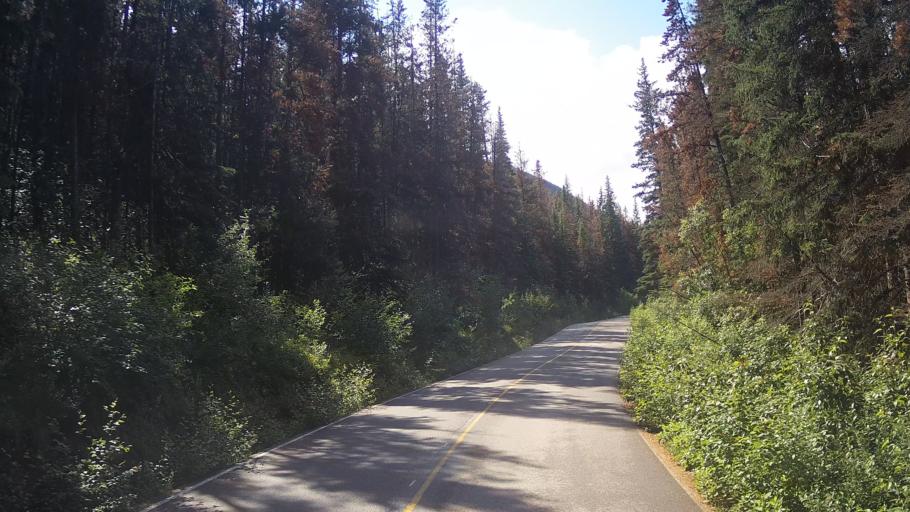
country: CA
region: Alberta
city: Jasper Park Lodge
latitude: 52.7669
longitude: -118.0371
